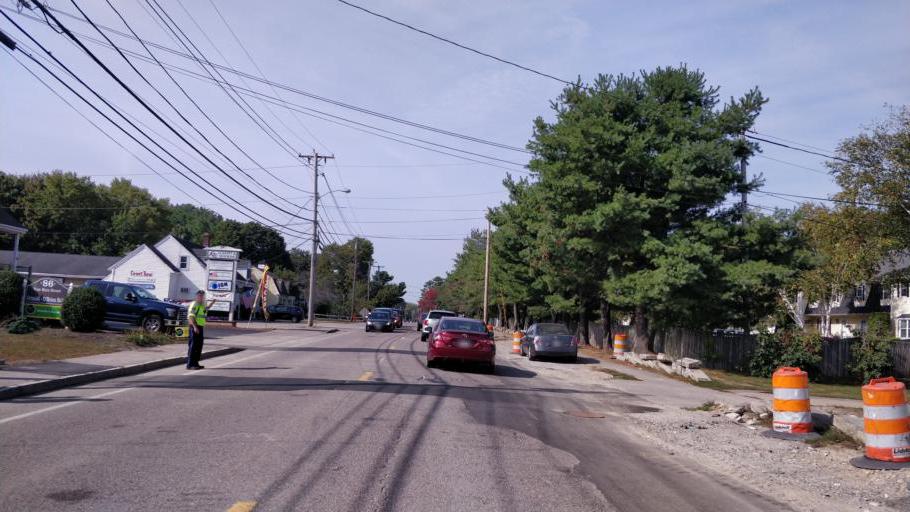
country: US
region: Massachusetts
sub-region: Bristol County
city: Norton
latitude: 41.9626
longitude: -71.1953
